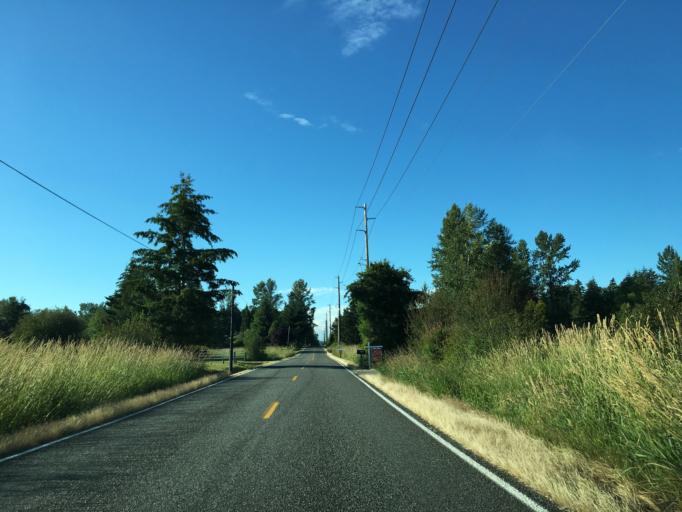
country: US
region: Washington
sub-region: Whatcom County
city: Birch Bay
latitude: 48.9312
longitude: -122.7044
